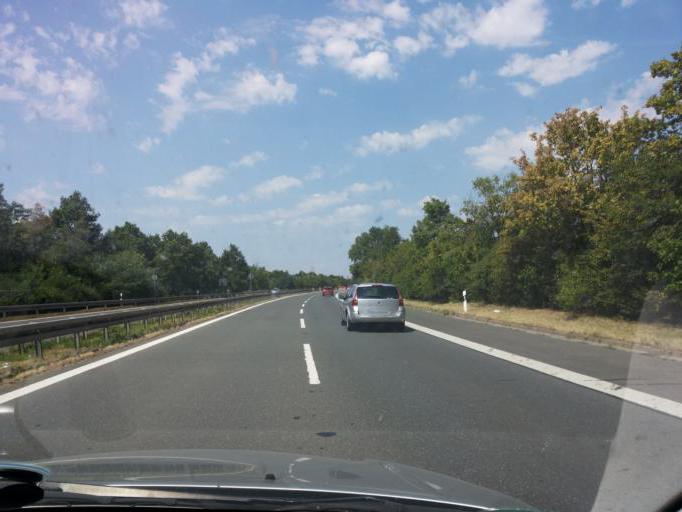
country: DE
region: Bavaria
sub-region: Regierungsbezirk Mittelfranken
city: Zirndorf
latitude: 49.4709
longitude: 10.9508
